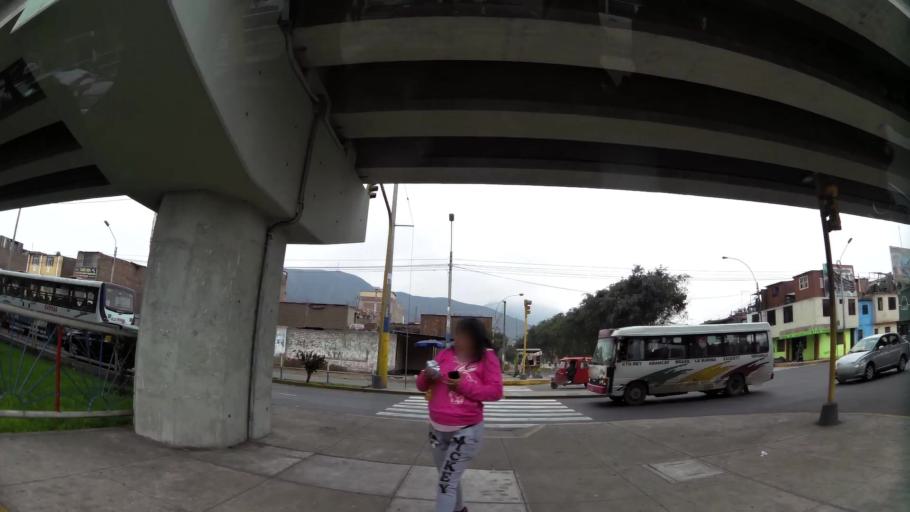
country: PE
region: Lima
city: Lima
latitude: -12.0232
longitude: -77.0095
